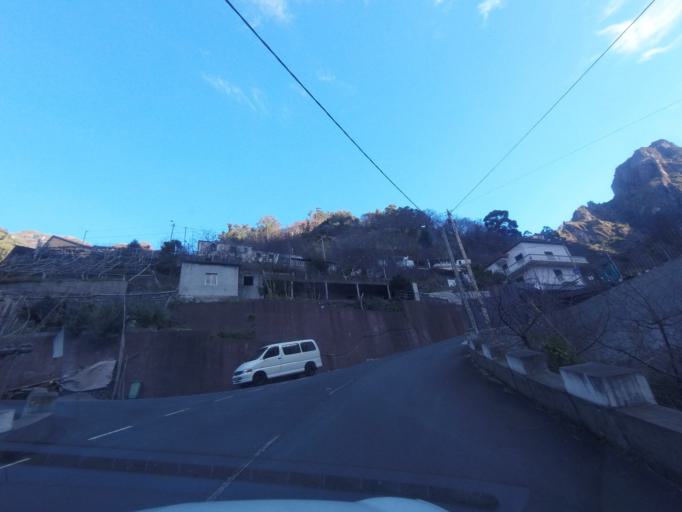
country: PT
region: Madeira
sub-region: Camara de Lobos
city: Curral das Freiras
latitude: 32.7452
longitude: -16.9635
